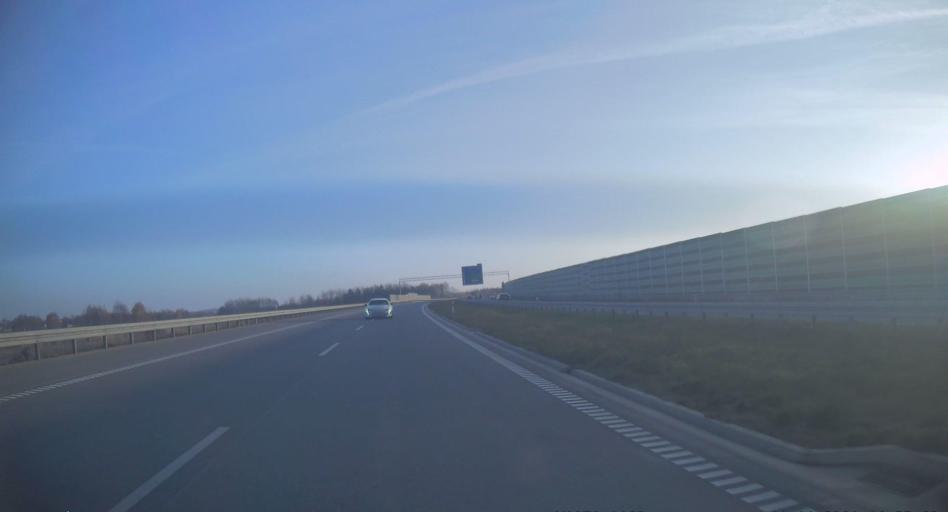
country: PL
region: Silesian Voivodeship
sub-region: Powiat tarnogorski
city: Ozarowice
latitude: 50.4676
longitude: 19.0565
